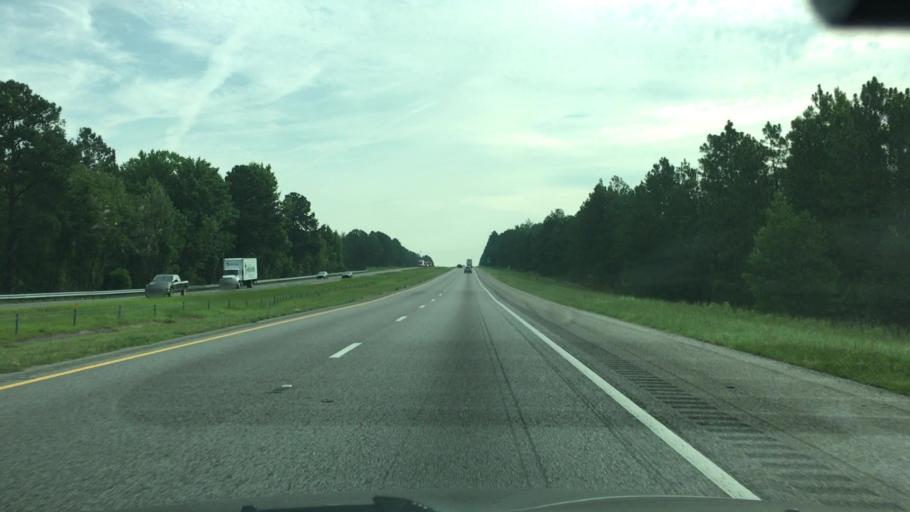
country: US
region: South Carolina
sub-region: Lexington County
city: Batesburg
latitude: 33.7363
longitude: -81.5486
